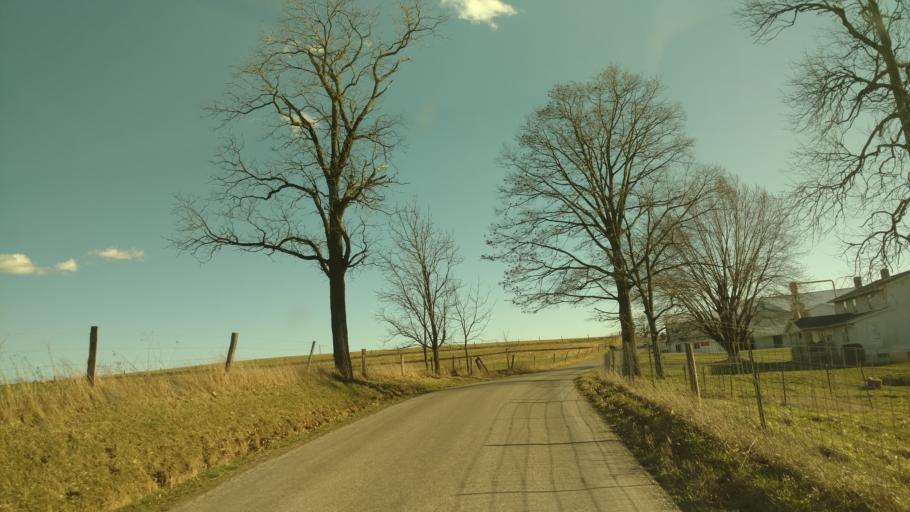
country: US
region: Ohio
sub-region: Tuscarawas County
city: Sugarcreek
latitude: 40.5935
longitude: -81.7614
